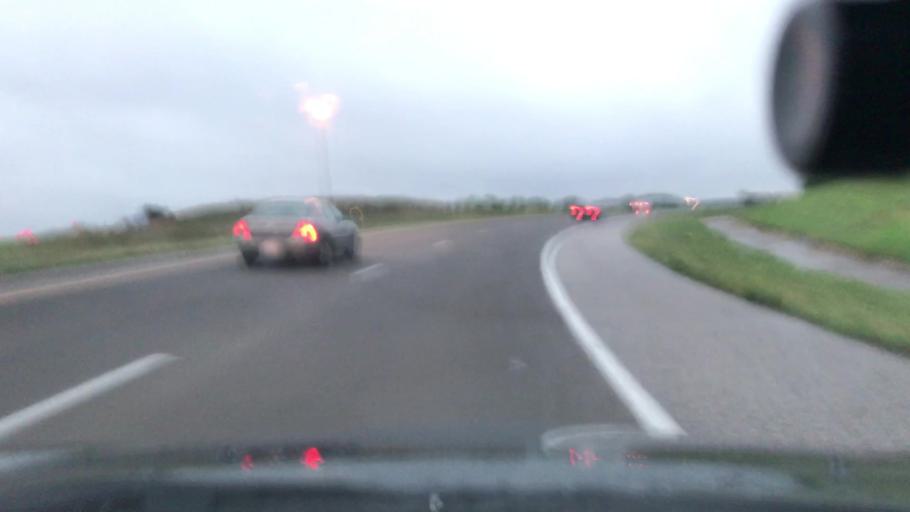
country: US
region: Missouri
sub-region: Saint Louis County
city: Maryland Heights
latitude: 38.6972
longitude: -90.4544
